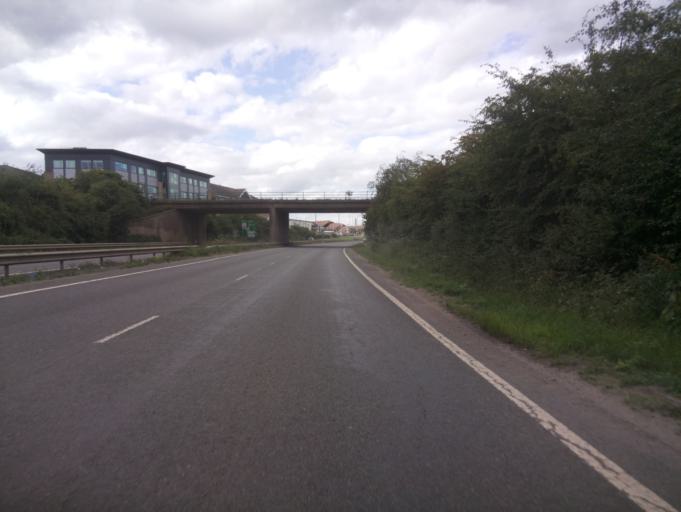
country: GB
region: England
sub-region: Warwickshire
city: Nuneaton
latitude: 52.5069
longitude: -1.4762
